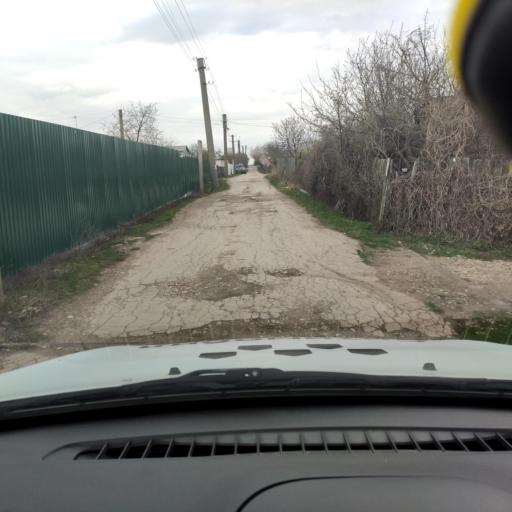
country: RU
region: Samara
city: Mezhdurechensk
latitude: 53.2443
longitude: 49.1533
